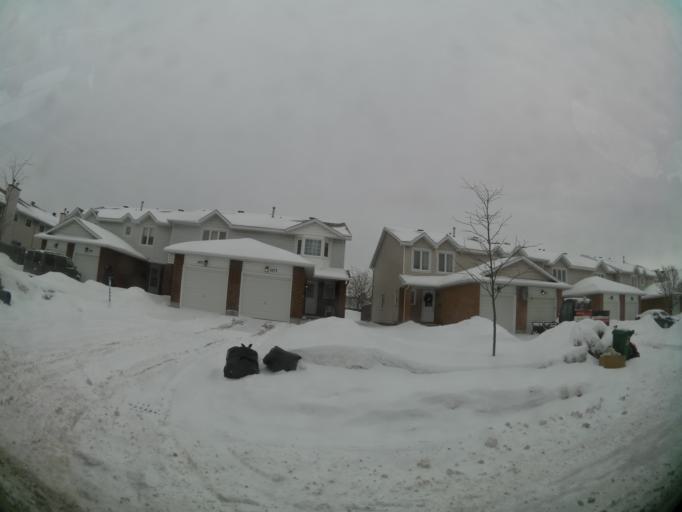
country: CA
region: Ontario
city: Ottawa
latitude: 45.3735
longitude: -75.6206
